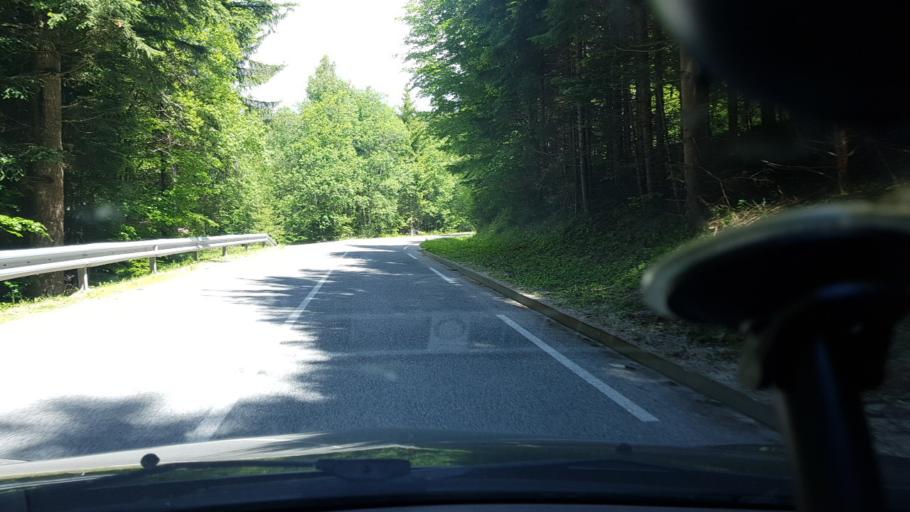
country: SI
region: Zrece
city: Zrece
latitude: 46.4392
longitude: 15.3645
